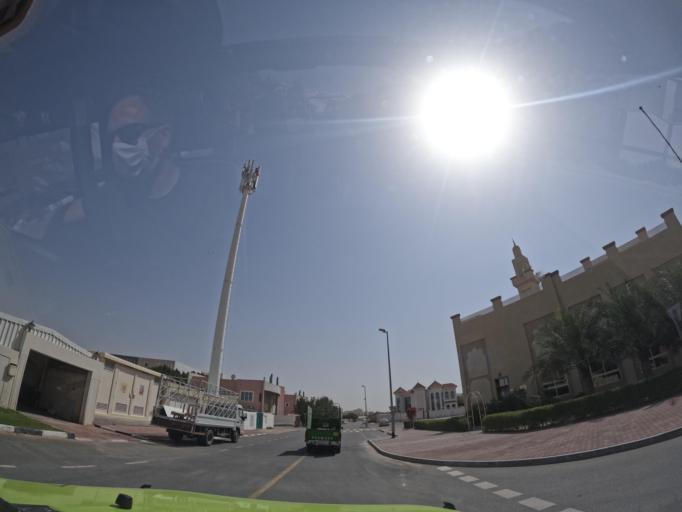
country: AE
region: Ash Shariqah
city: Sharjah
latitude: 25.2063
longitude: 55.4234
